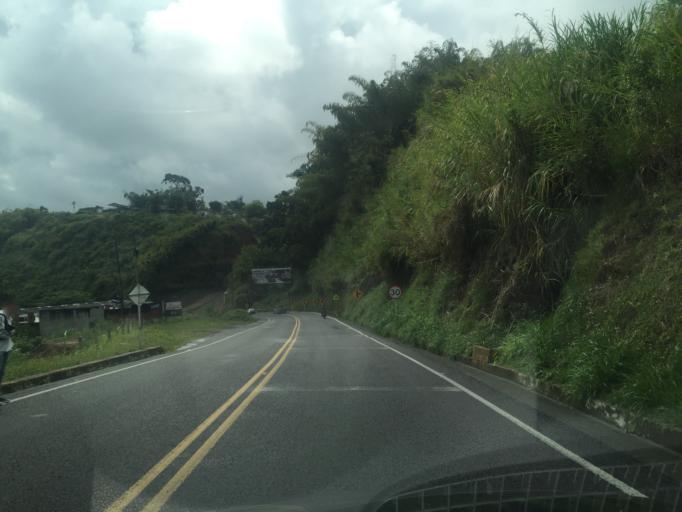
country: CO
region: Risaralda
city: Pereira
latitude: 4.7836
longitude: -75.6979
